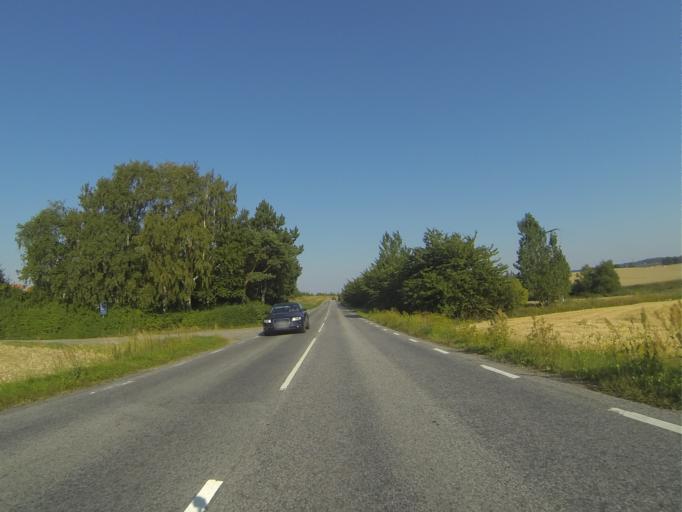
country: SE
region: Skane
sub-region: Malmo
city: Oxie
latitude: 55.5774
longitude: 13.1618
